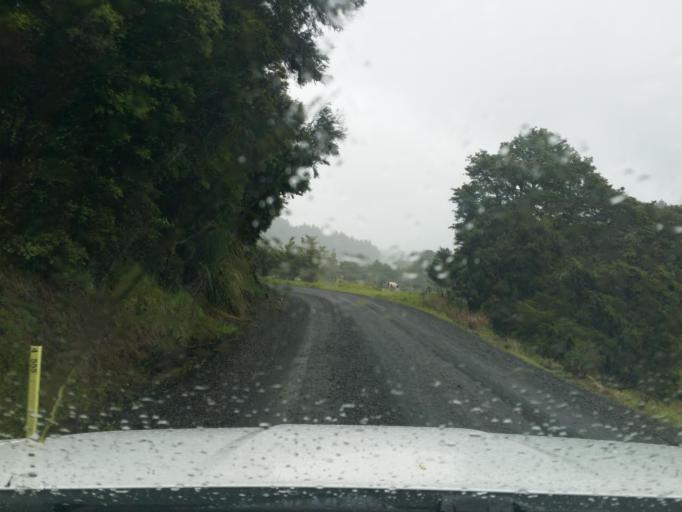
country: NZ
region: Northland
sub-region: Kaipara District
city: Dargaville
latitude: -35.8075
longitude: 173.9882
